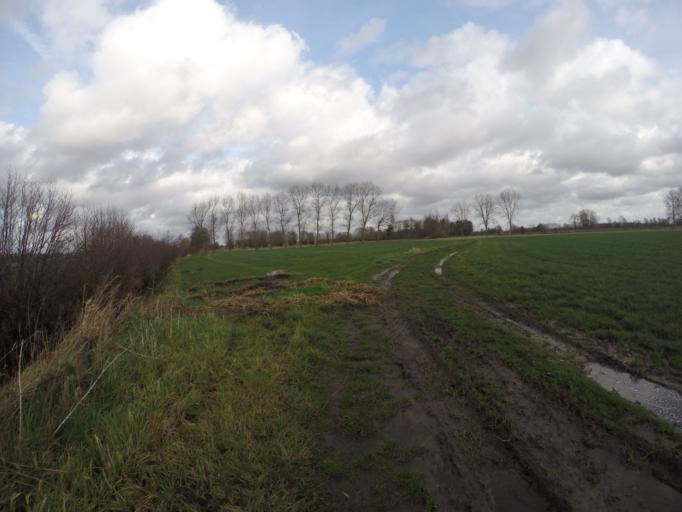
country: BE
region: Flanders
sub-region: Provincie Oost-Vlaanderen
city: Knesselare
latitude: 51.1220
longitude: 3.4063
